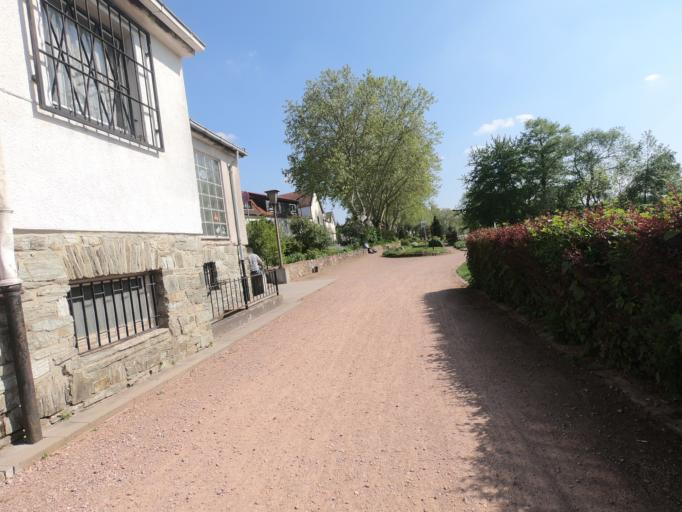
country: DE
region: Hesse
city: Kelsterbach
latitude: 50.0697
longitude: 8.5279
